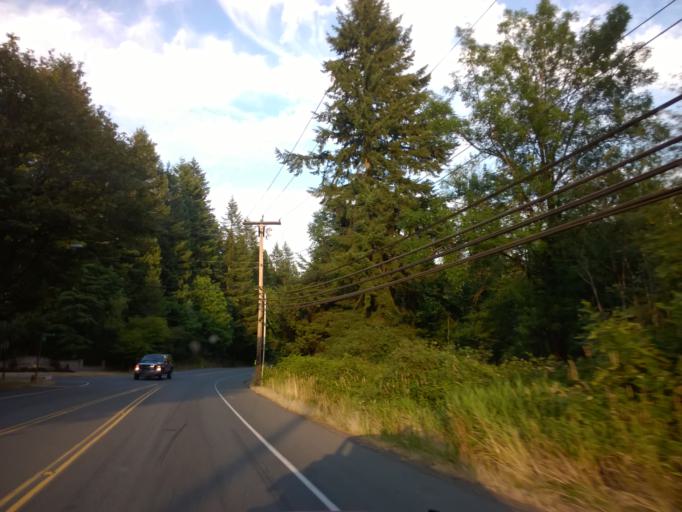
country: US
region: Washington
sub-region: King County
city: Cottage Lake
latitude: 47.7547
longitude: -122.0776
